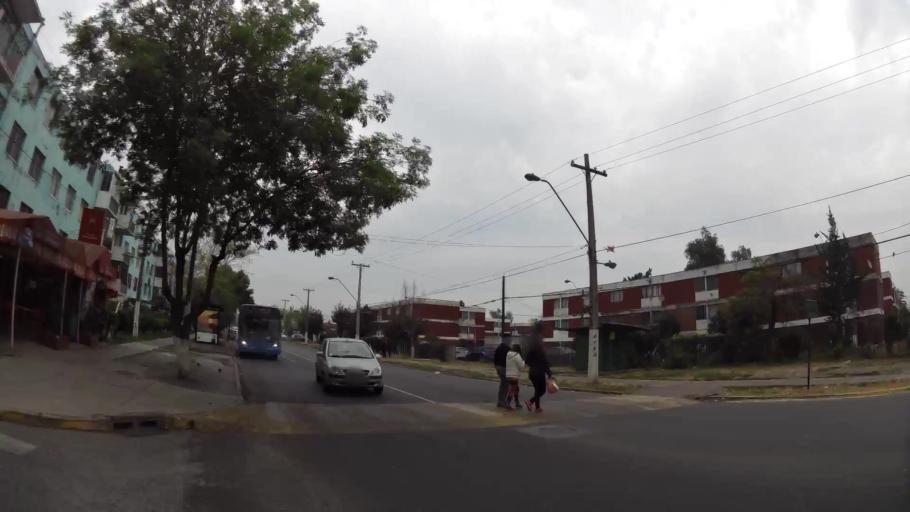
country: CL
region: Santiago Metropolitan
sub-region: Provincia de Santiago
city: Villa Presidente Frei, Nunoa, Santiago, Chile
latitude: -33.4869
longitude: -70.6062
